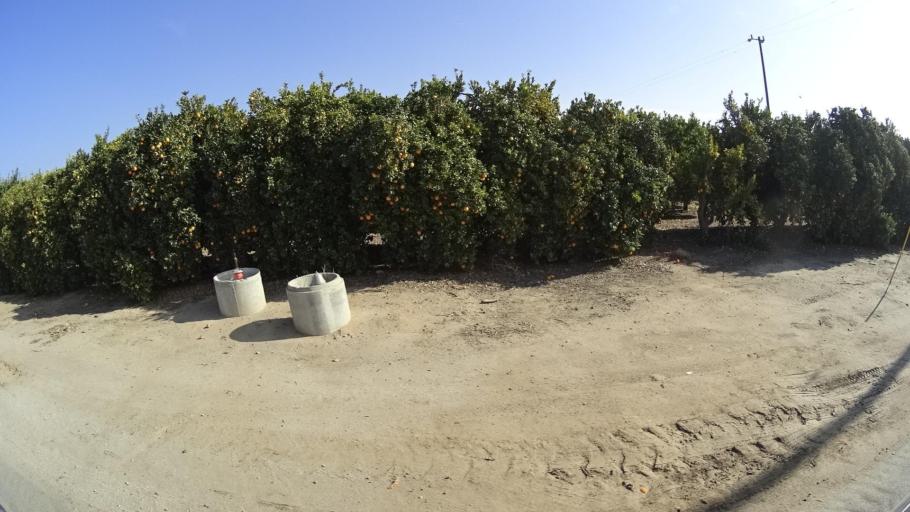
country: US
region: California
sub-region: Kern County
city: McFarland
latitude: 35.6095
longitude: -119.1865
